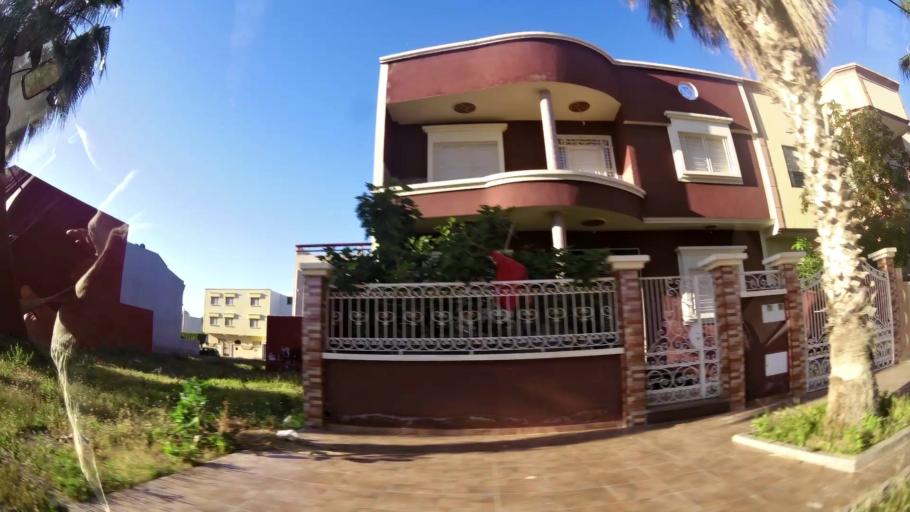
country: MA
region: Oriental
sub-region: Berkane-Taourirt
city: Madagh
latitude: 35.0843
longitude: -2.2477
